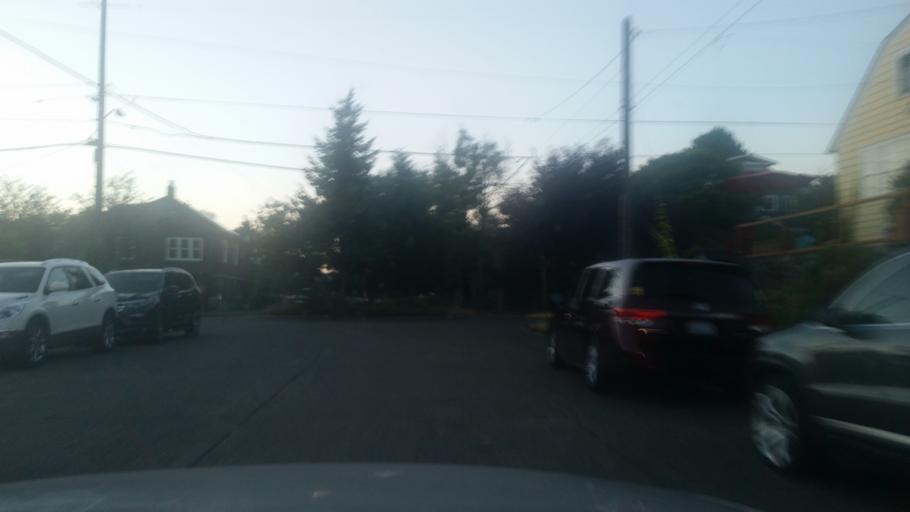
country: US
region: Washington
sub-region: King County
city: Shoreline
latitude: 47.6852
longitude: -122.3633
